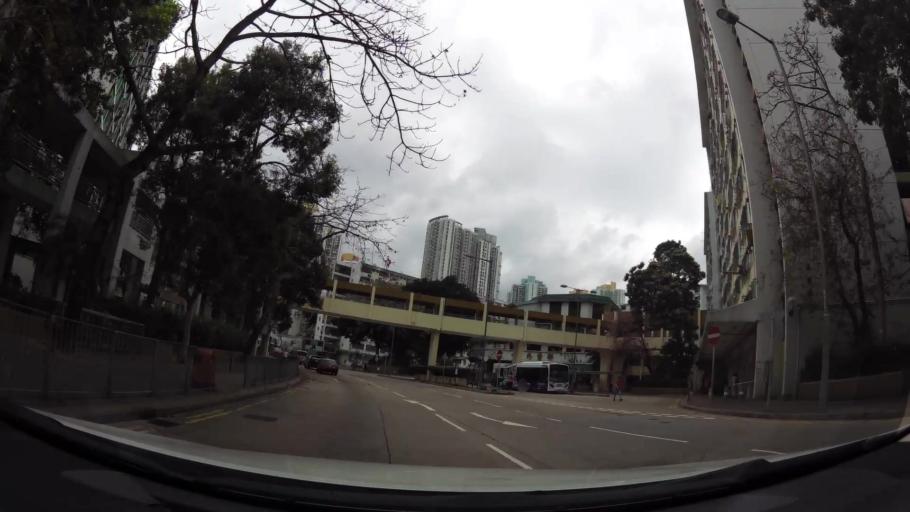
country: HK
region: Sham Shui Po
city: Sham Shui Po
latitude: 22.3313
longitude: 114.1712
